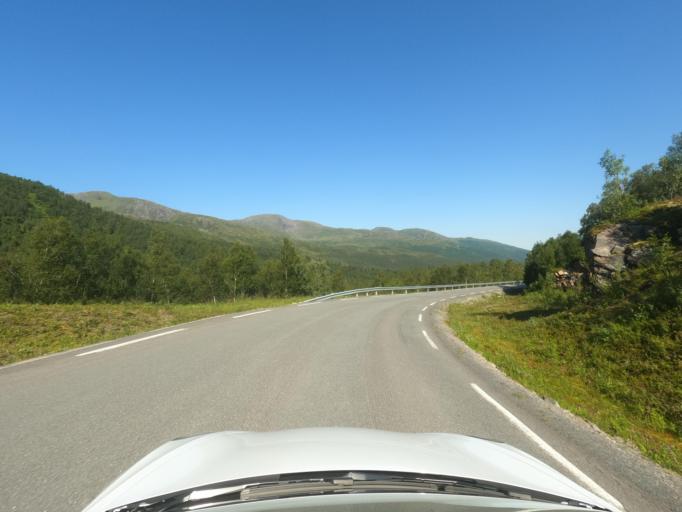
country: NO
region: Troms
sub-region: Skanland
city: Evenskjer
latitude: 68.3296
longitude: 16.5437
